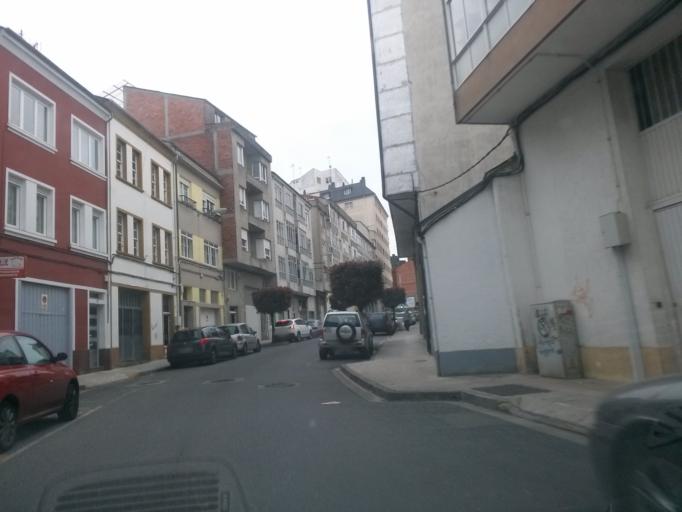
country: ES
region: Galicia
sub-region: Provincia de Lugo
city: Lugo
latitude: 43.0236
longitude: -7.5638
